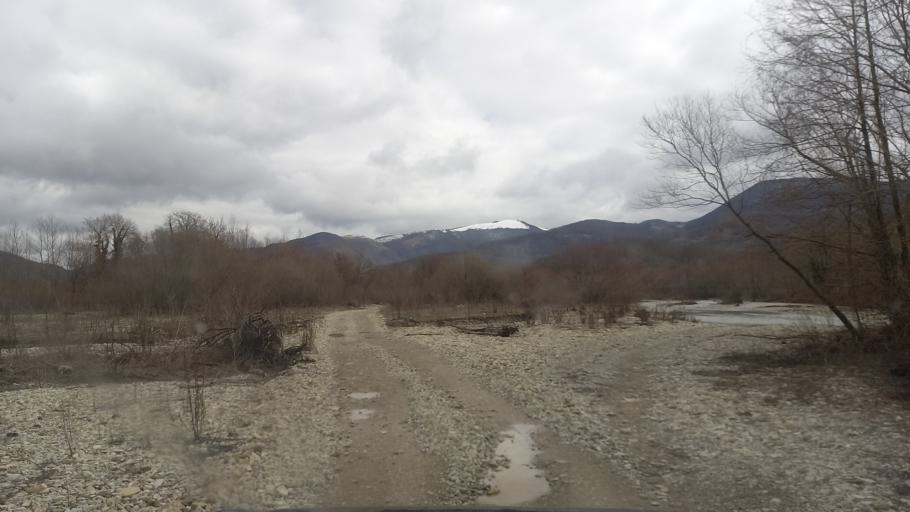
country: RU
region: Krasnodarskiy
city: Pshada
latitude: 44.4907
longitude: 38.4129
